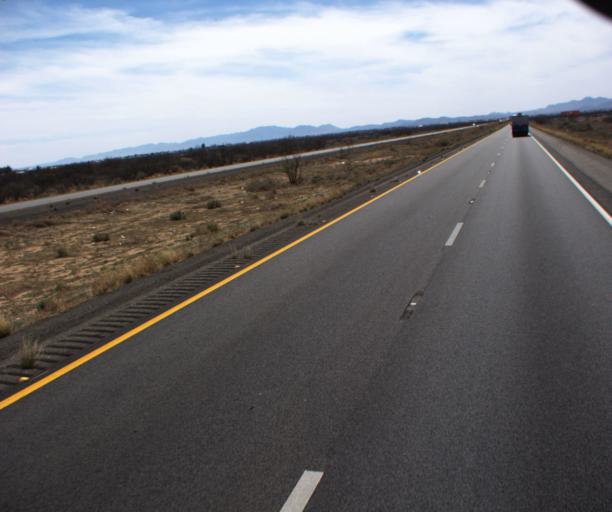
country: US
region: Arizona
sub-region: Cochise County
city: Willcox
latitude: 32.2959
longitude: -109.8116
